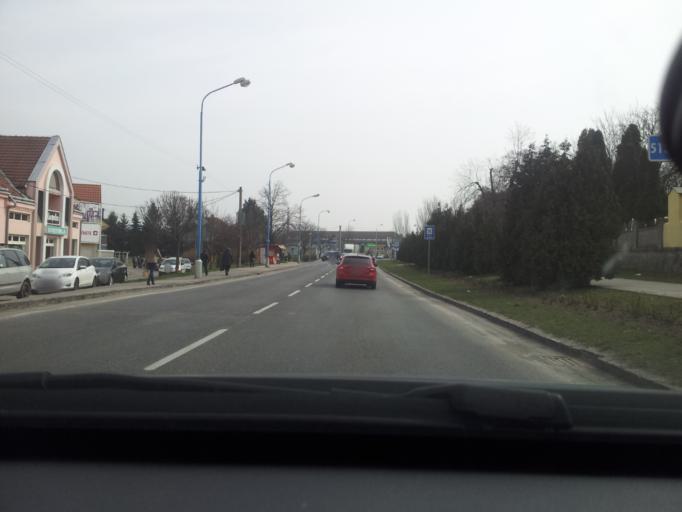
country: SK
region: Trnavsky
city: Hlohovec
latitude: 48.4253
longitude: 17.8037
